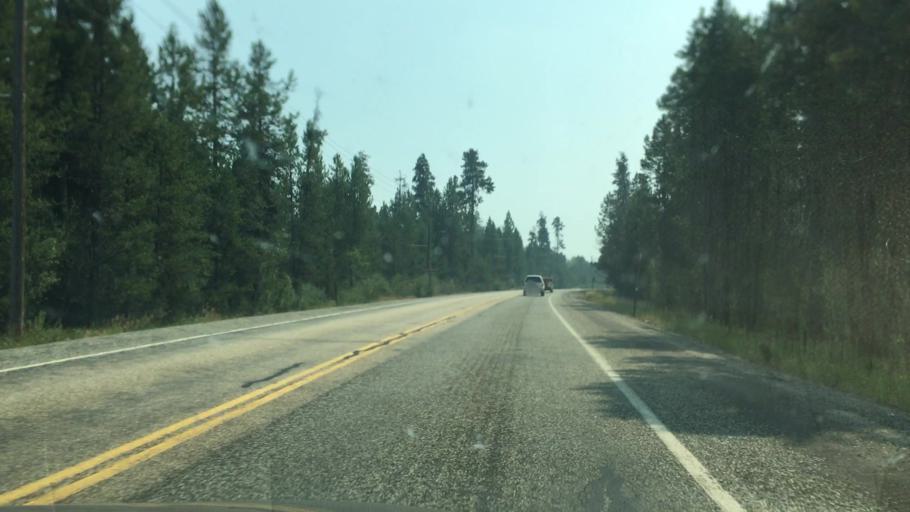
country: US
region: Idaho
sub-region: Valley County
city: Cascade
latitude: 44.4038
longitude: -116.0004
